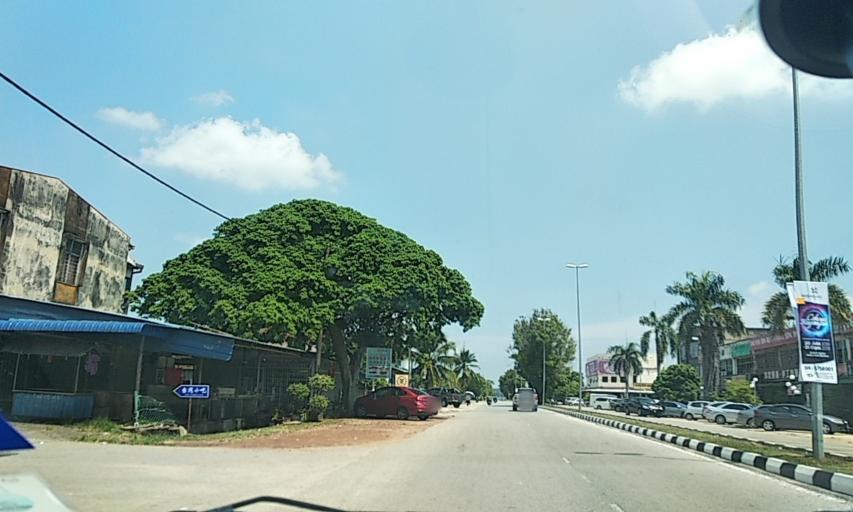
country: MY
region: Kedah
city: Sungai Petani
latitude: 5.6361
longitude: 100.4734
